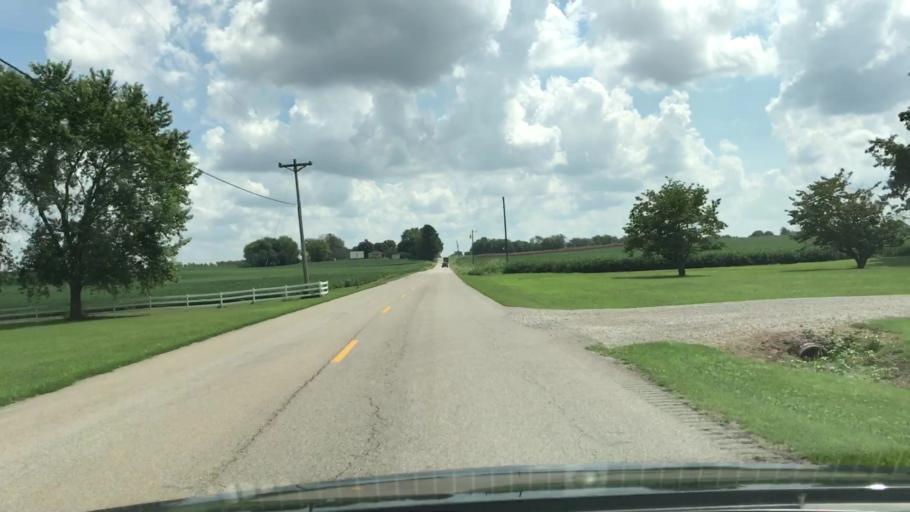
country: US
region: Kentucky
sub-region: Todd County
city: Guthrie
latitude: 36.7136
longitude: -87.0614
